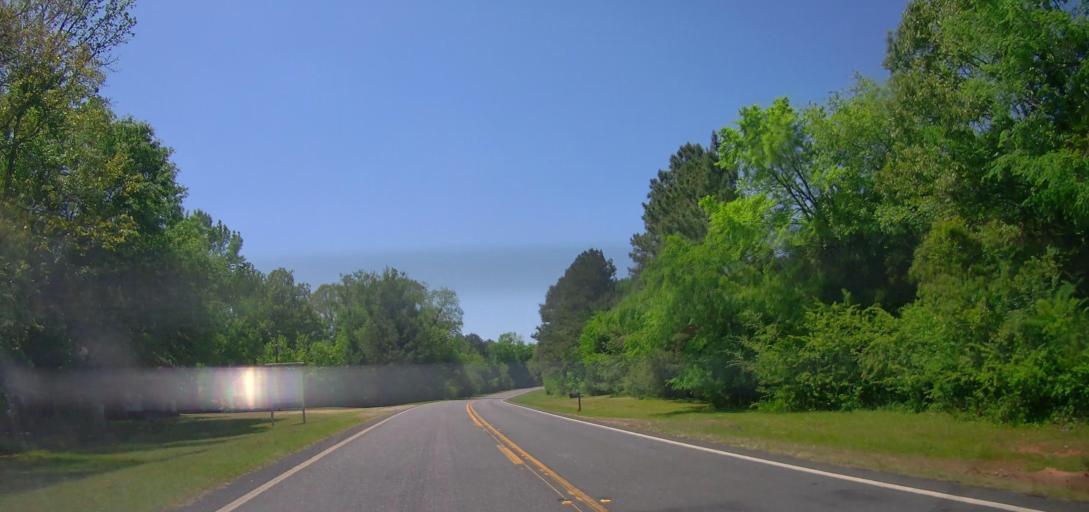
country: US
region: Georgia
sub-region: Putnam County
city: Eatonton
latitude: 33.2236
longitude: -83.5040
